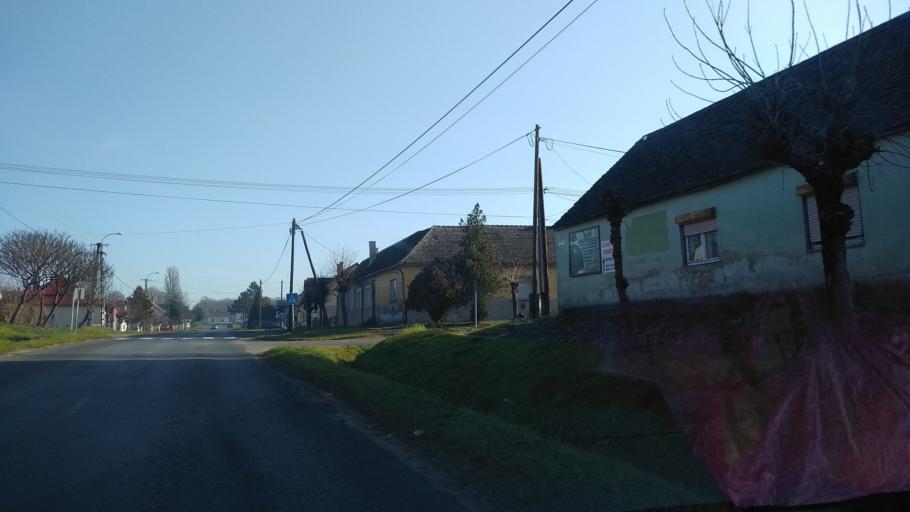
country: HU
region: Somogy
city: Barcs
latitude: 45.9616
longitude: 17.4815
